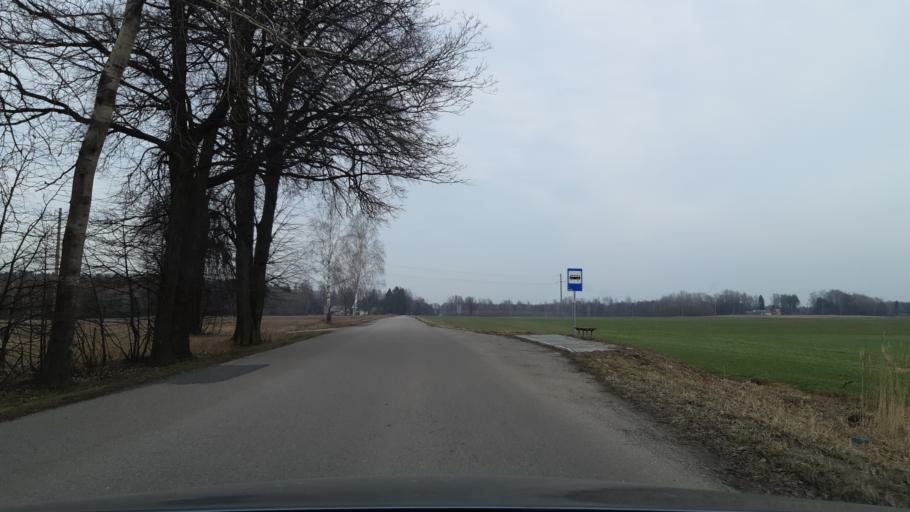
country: LT
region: Marijampoles apskritis
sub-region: Marijampole Municipality
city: Marijampole
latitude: 54.7279
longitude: 23.3365
